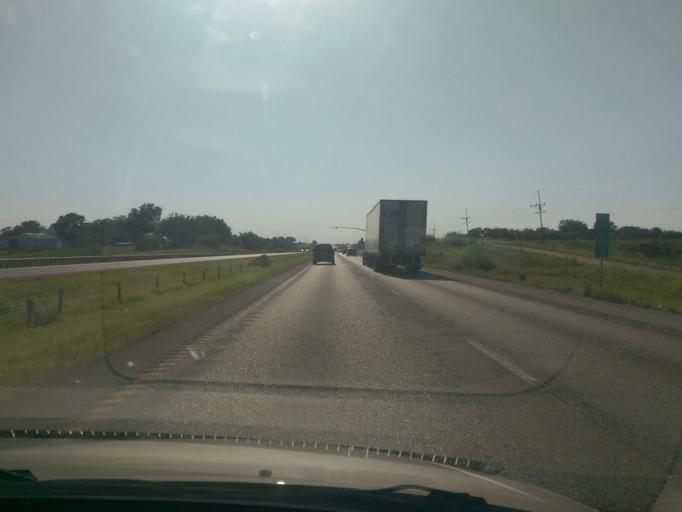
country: US
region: Missouri
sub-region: Lafayette County
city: Odessa
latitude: 39.0034
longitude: -93.8280
